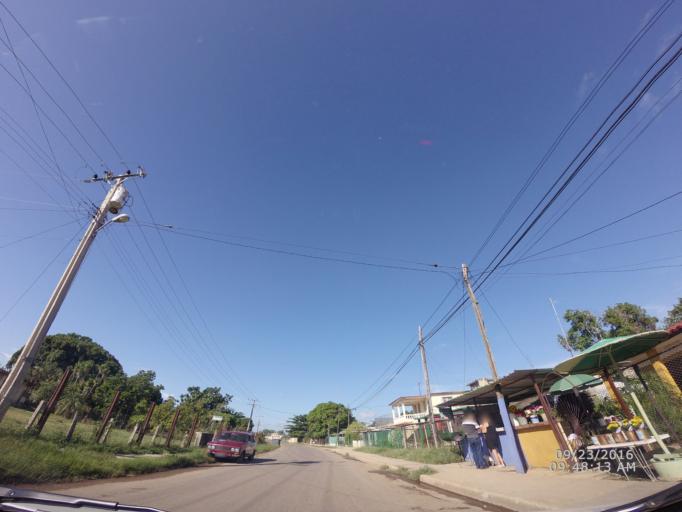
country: CU
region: La Habana
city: Santiago de las Vegas
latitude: 22.9518
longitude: -82.4188
